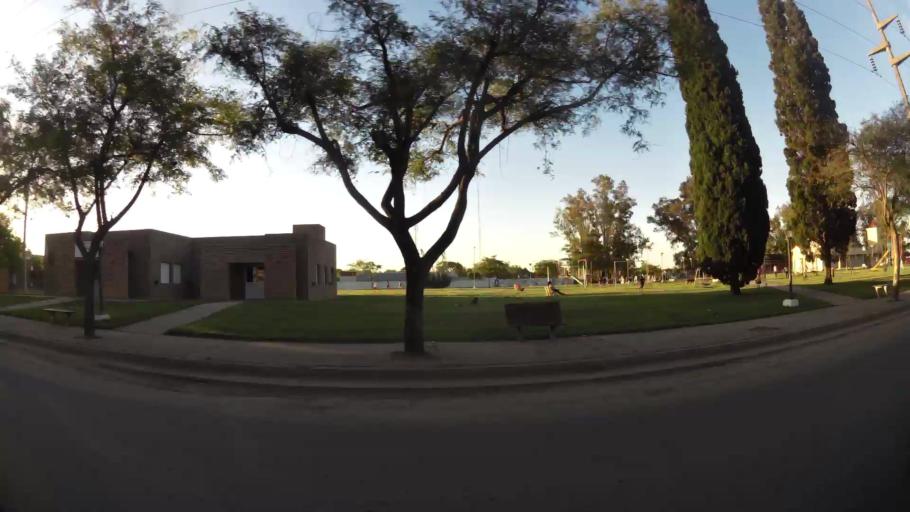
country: AR
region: Cordoba
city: La Playosa
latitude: -32.1006
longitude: -63.0321
